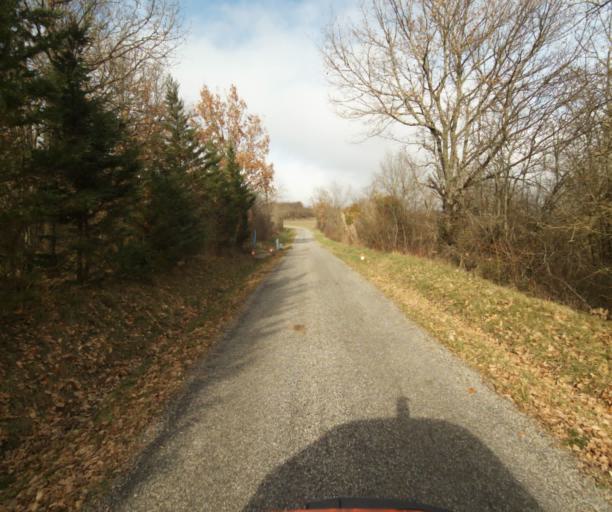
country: FR
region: Languedoc-Roussillon
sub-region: Departement de l'Aude
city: Belpech
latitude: 43.1621
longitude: 1.7382
